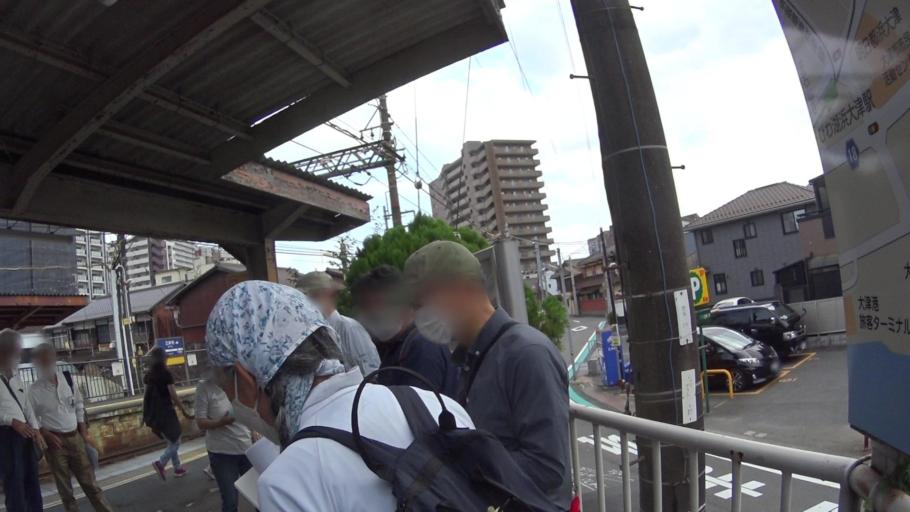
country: JP
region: Shiga Prefecture
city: Nagahama
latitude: 35.3879
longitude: 136.2268
